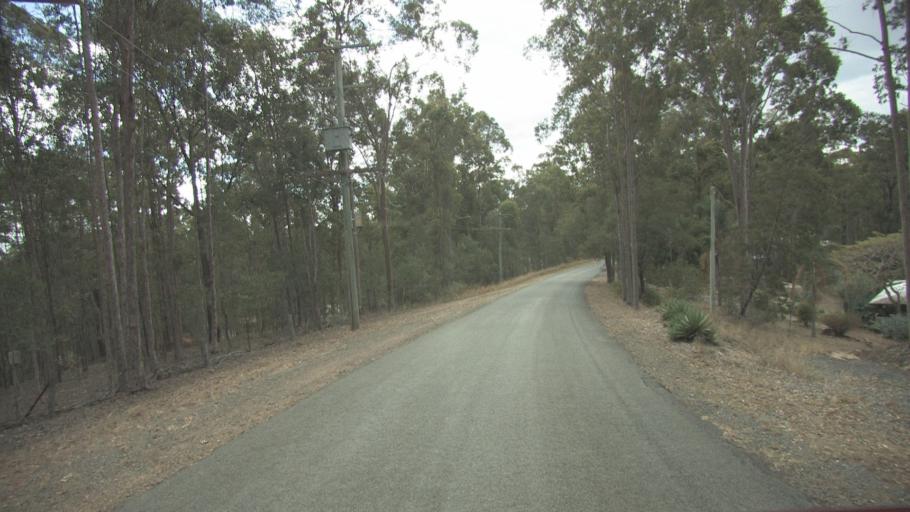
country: AU
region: Queensland
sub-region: Logan
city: Cedar Vale
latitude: -27.8947
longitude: 153.0248
